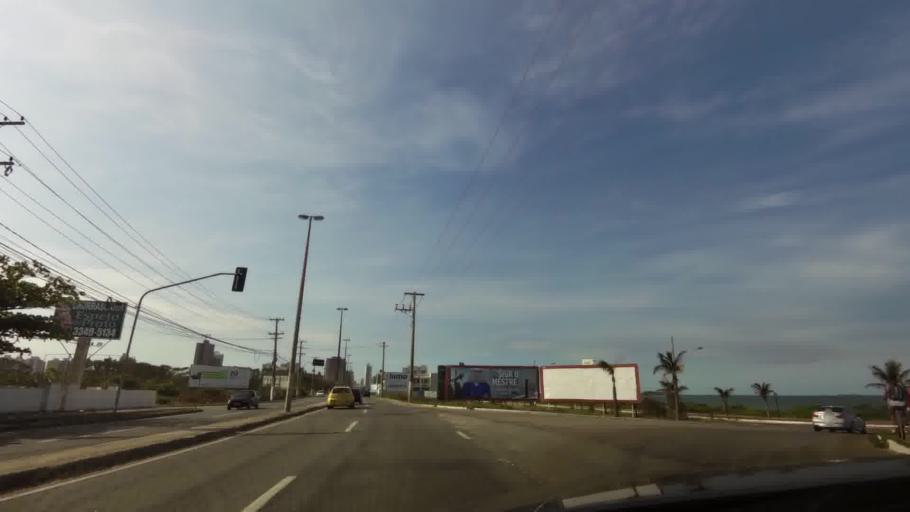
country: BR
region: Espirito Santo
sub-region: Vila Velha
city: Vila Velha
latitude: -20.3905
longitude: -40.3144
